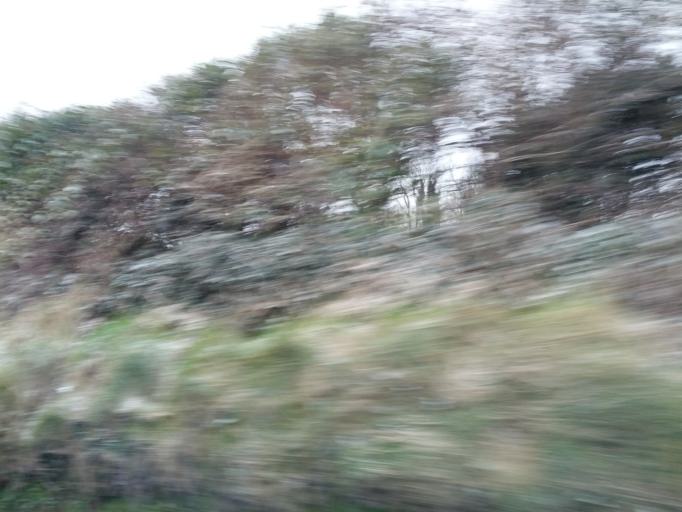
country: IE
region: Connaught
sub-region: County Galway
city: Oranmore
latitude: 53.2382
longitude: -8.8664
